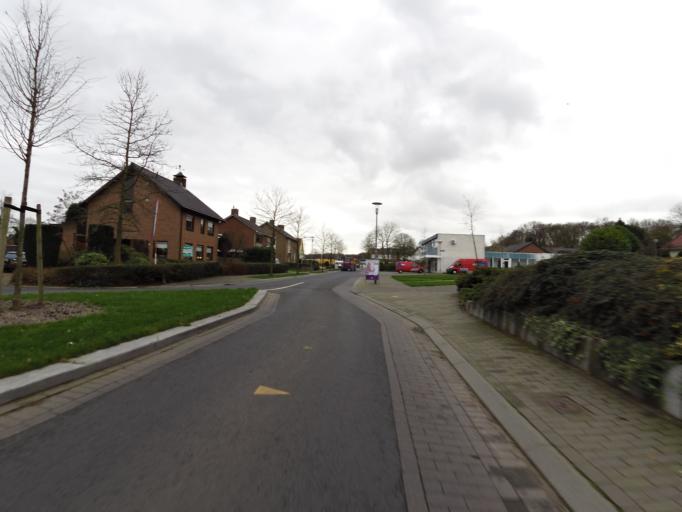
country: NL
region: Gelderland
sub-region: Gemeente Montferland
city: s-Heerenberg
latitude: 51.8996
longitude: 6.2575
